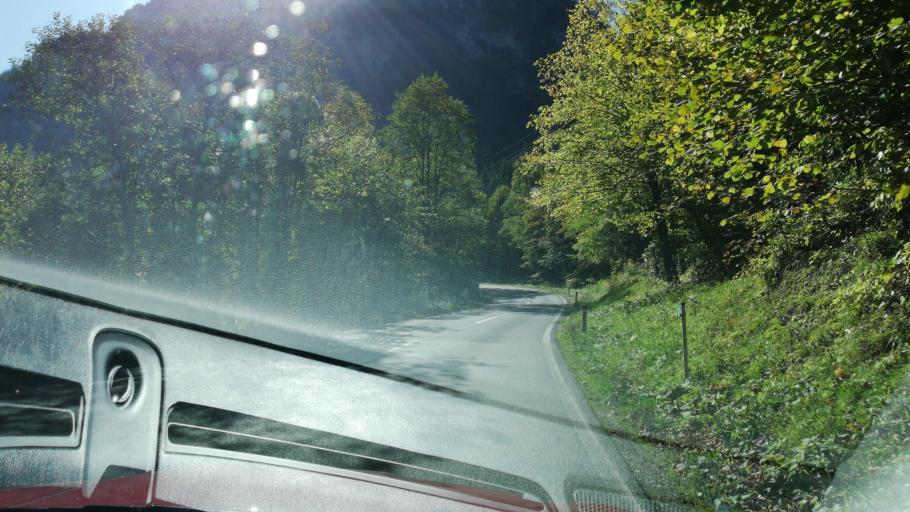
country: AT
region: Styria
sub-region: Politischer Bezirk Leoben
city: Eisenerz
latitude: 47.5786
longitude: 14.8274
